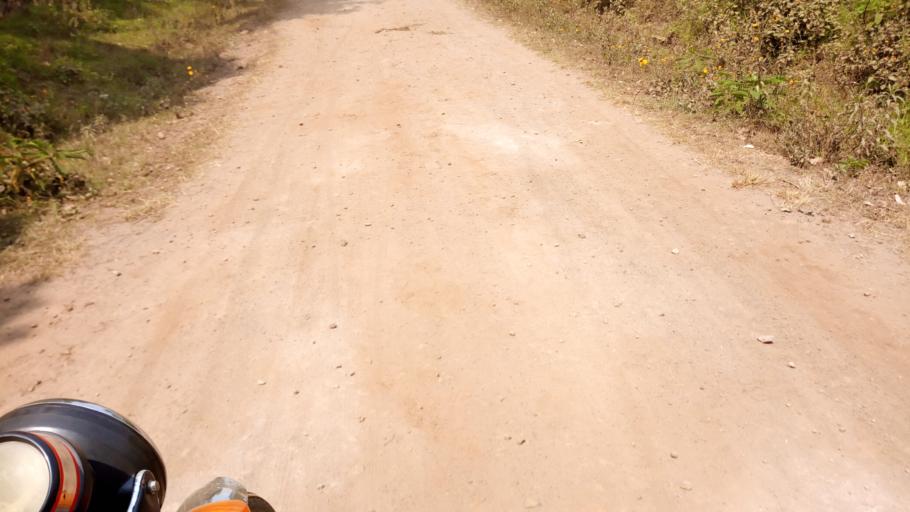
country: UG
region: Western Region
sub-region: Kisoro District
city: Kisoro
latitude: -1.3146
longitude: 29.7160
